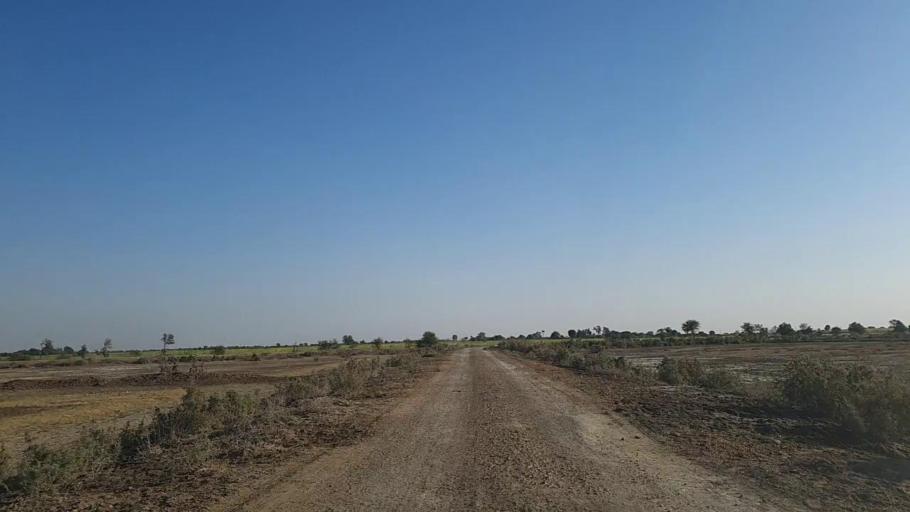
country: PK
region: Sindh
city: Naukot
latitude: 24.9766
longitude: 69.3802
